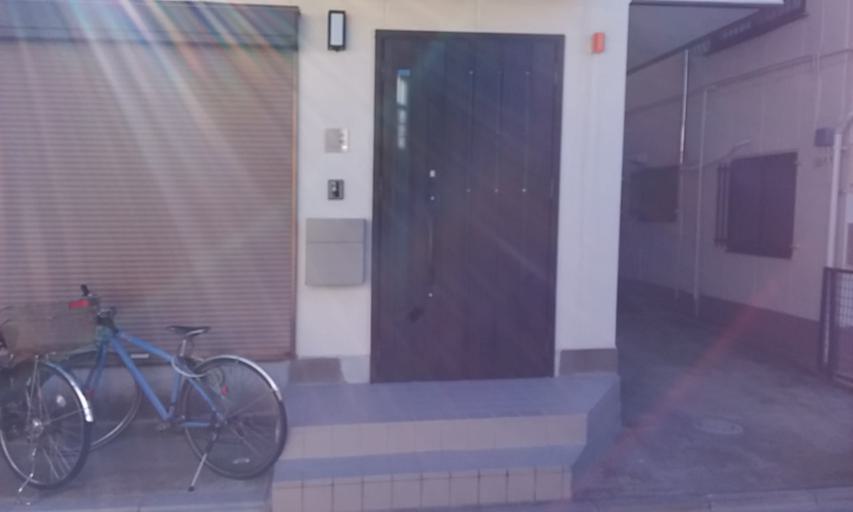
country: JP
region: Tokyo
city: Tokyo
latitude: 35.7230
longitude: 139.7427
